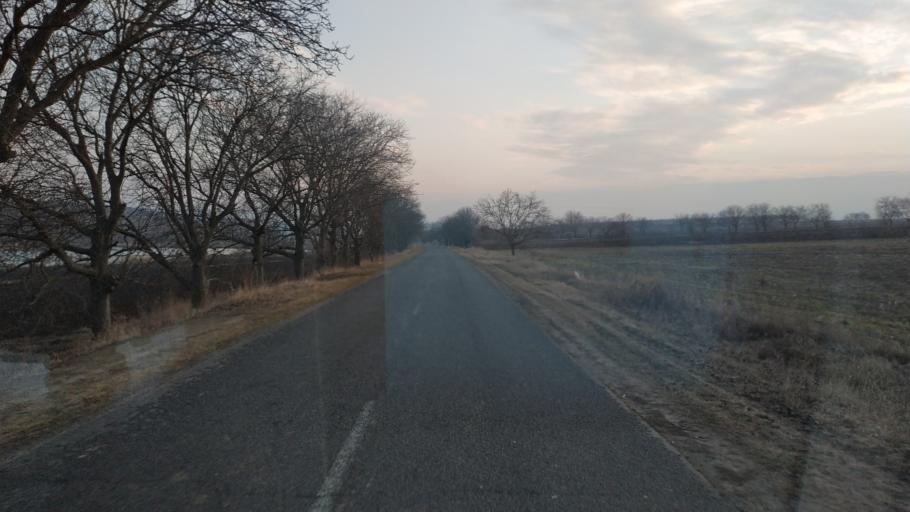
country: MD
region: Hincesti
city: Dancu
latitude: 46.6991
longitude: 28.3371
